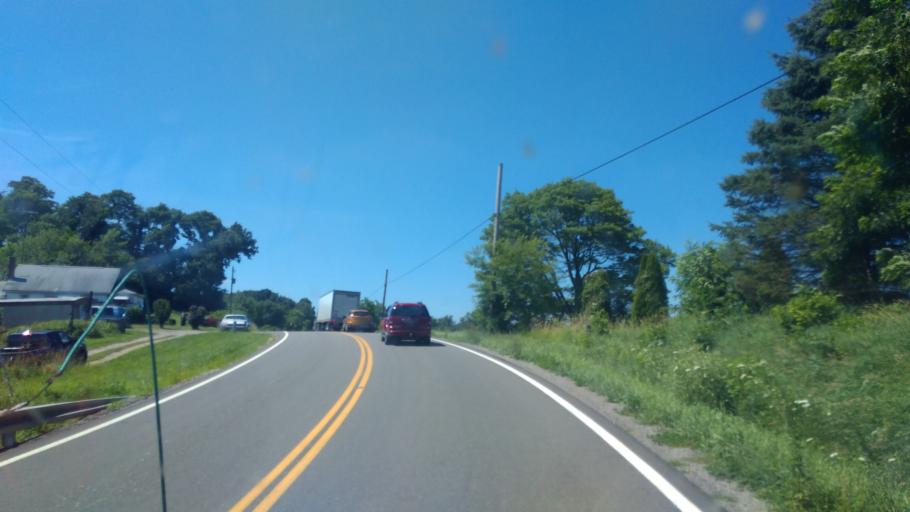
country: US
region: Ohio
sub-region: Carroll County
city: Carrollton
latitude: 40.5079
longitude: -80.9871
